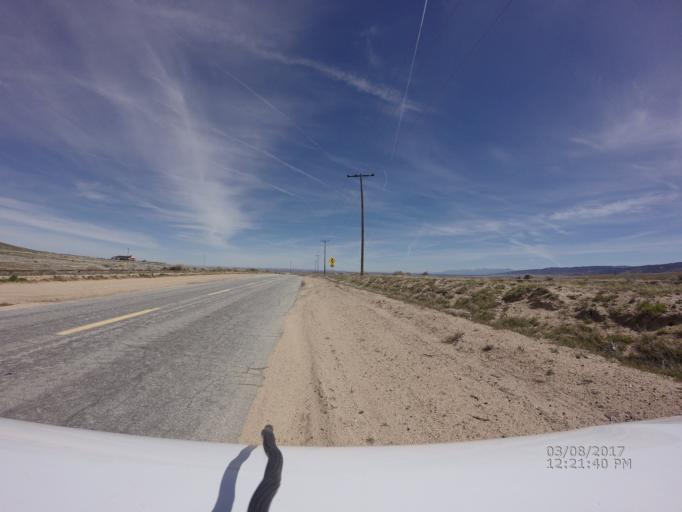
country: US
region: California
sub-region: Los Angeles County
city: Green Valley
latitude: 34.7248
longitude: -118.3932
